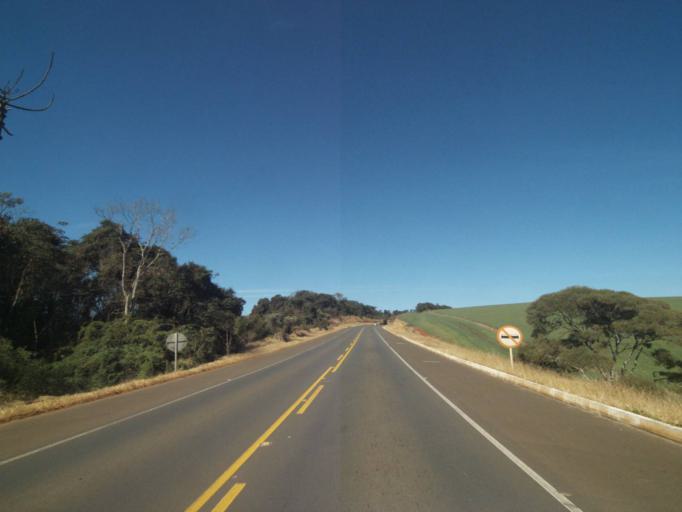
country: BR
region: Parana
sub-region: Tibagi
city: Tibagi
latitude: -24.7126
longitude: -50.4496
